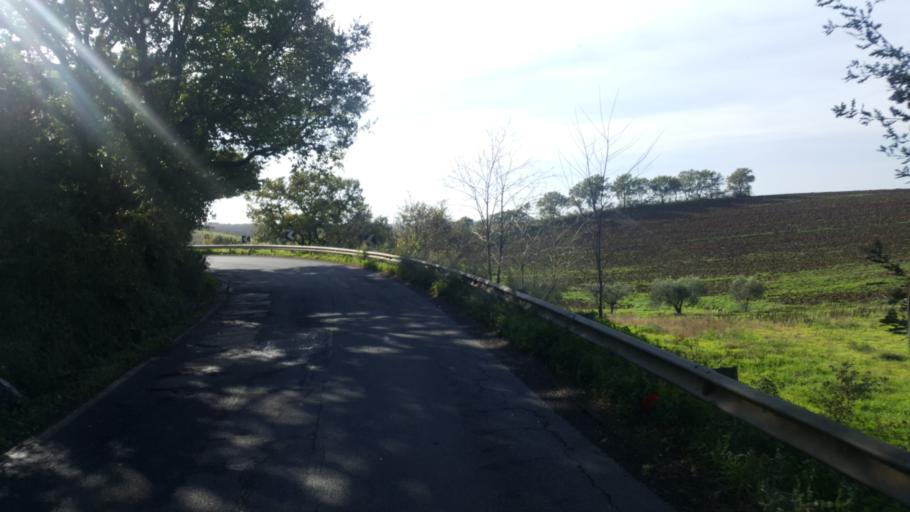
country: IT
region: Latium
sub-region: Citta metropolitana di Roma Capitale
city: Mantiglia di Ardea
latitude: 41.6521
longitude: 12.6221
